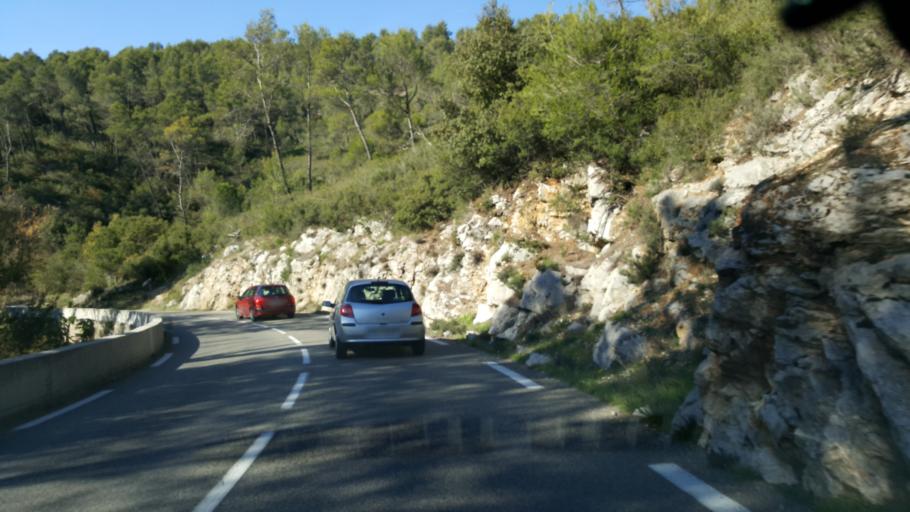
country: FR
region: Provence-Alpes-Cote d'Azur
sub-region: Departement du Var
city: Saint-Zacharie
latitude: 43.3848
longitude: 5.7353
